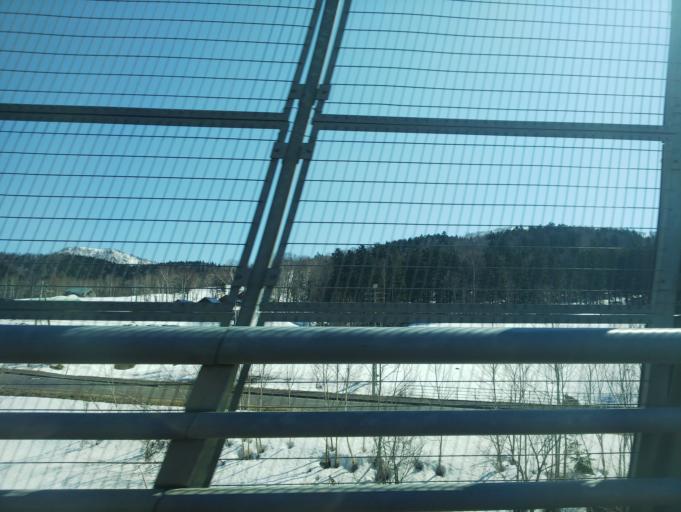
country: JP
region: Hokkaido
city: Nayoro
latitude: 44.7205
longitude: 142.2704
